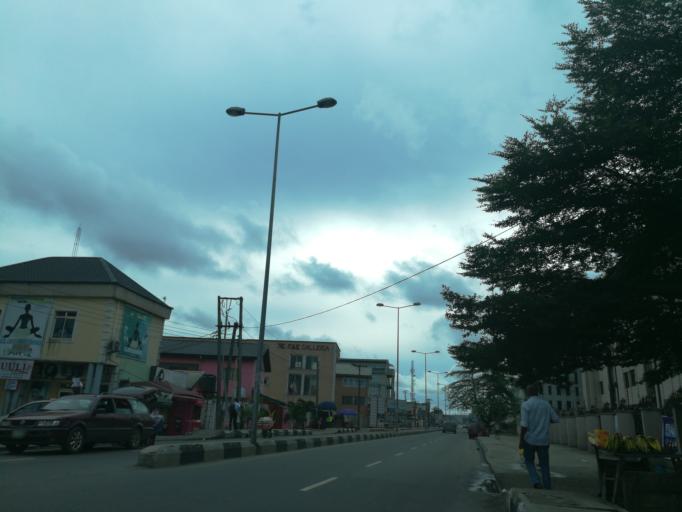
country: NG
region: Rivers
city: Port Harcourt
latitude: 4.8151
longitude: 6.9907
